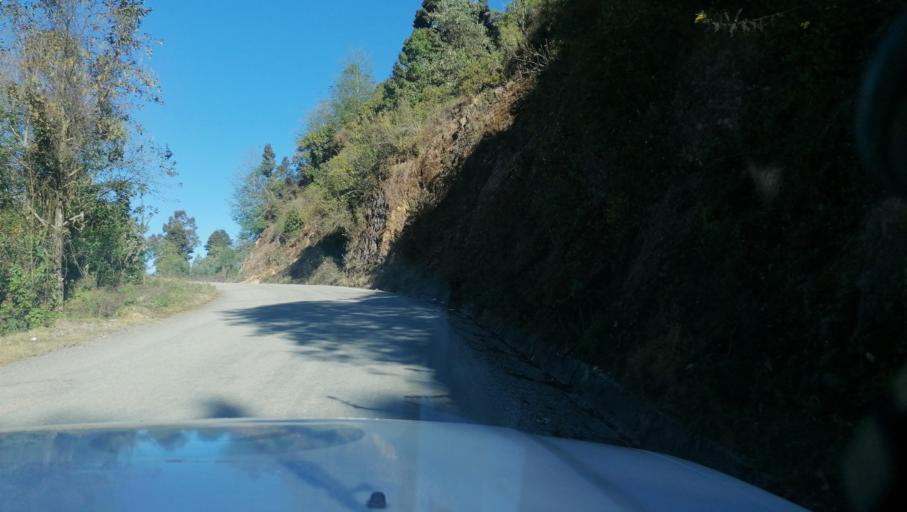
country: MX
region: Chiapas
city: Motozintla de Mendoza
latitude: 15.2667
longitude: -92.2263
